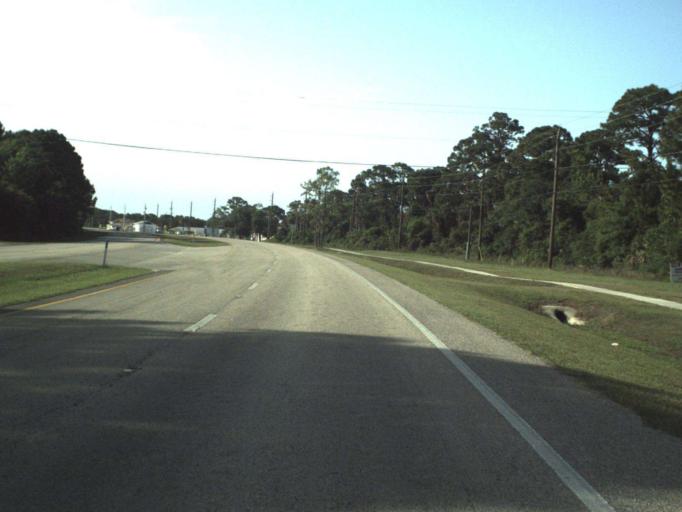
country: US
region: Florida
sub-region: Volusia County
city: Oak Hill
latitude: 28.8727
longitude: -80.8515
